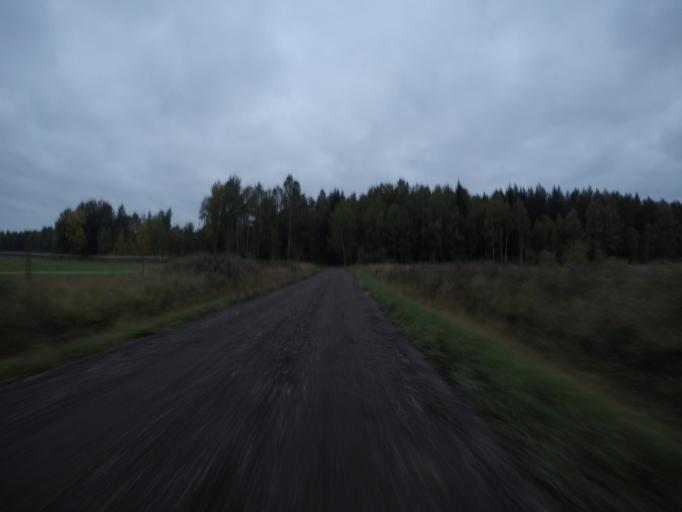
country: SE
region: Vaestmanland
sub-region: Kungsors Kommun
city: Kungsoer
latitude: 59.3965
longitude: 16.1146
